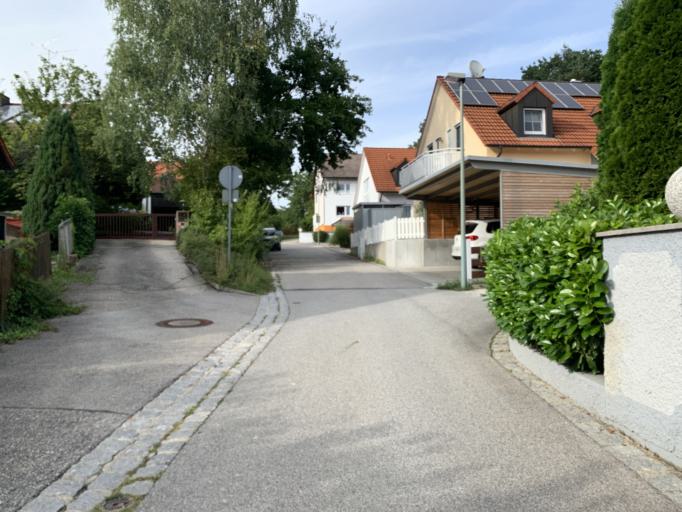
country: DE
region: Bavaria
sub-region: Upper Bavaria
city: Freising
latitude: 48.4021
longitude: 11.7198
